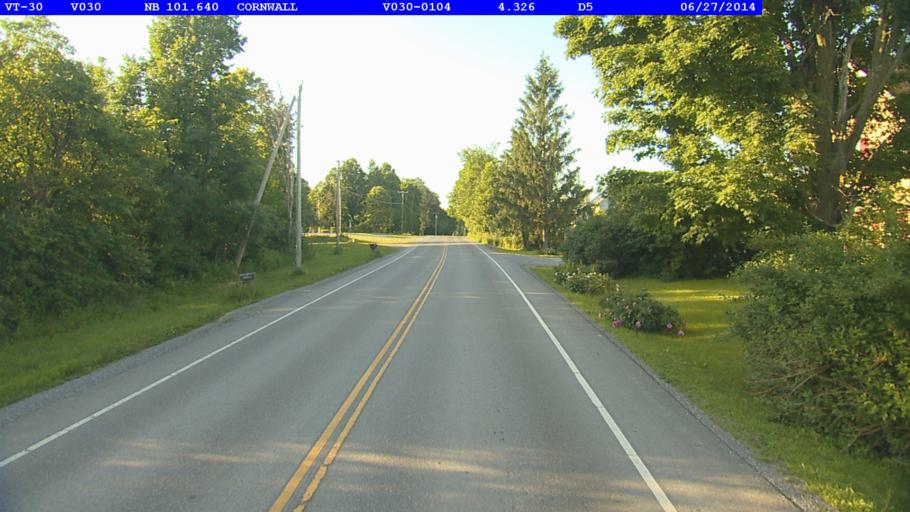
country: US
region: Vermont
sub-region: Addison County
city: Middlebury (village)
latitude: 43.9697
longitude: -73.2066
